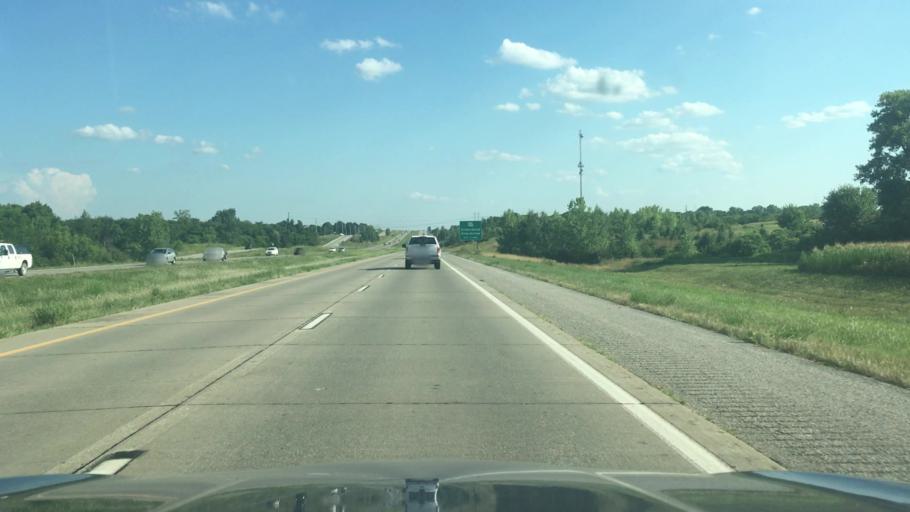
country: US
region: Missouri
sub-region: Jackson County
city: Greenwood
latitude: 38.8725
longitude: -94.3749
